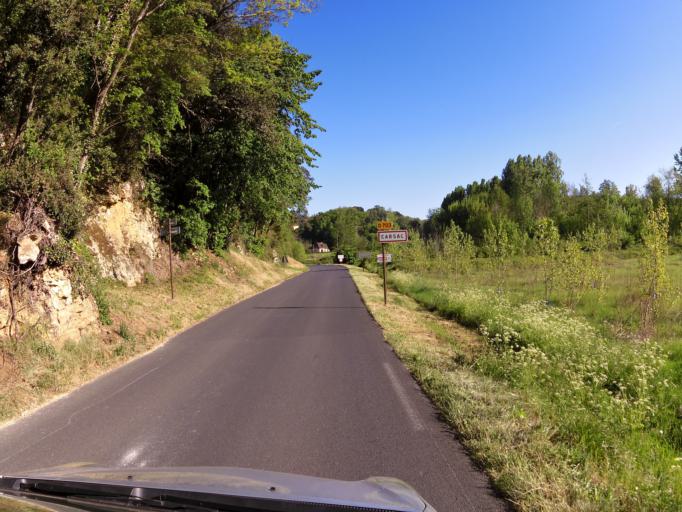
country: FR
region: Aquitaine
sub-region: Departement de la Dordogne
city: Carsac-Aillac
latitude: 44.8413
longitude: 1.2693
